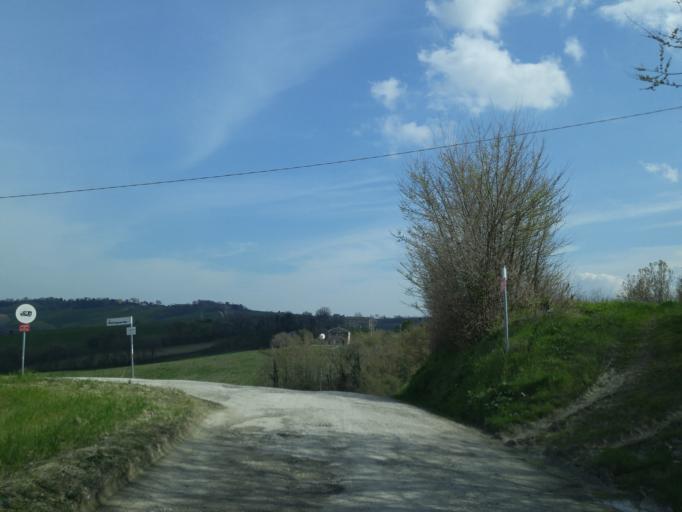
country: IT
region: The Marches
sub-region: Provincia di Pesaro e Urbino
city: Villanova
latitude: 43.7261
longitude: 12.9319
